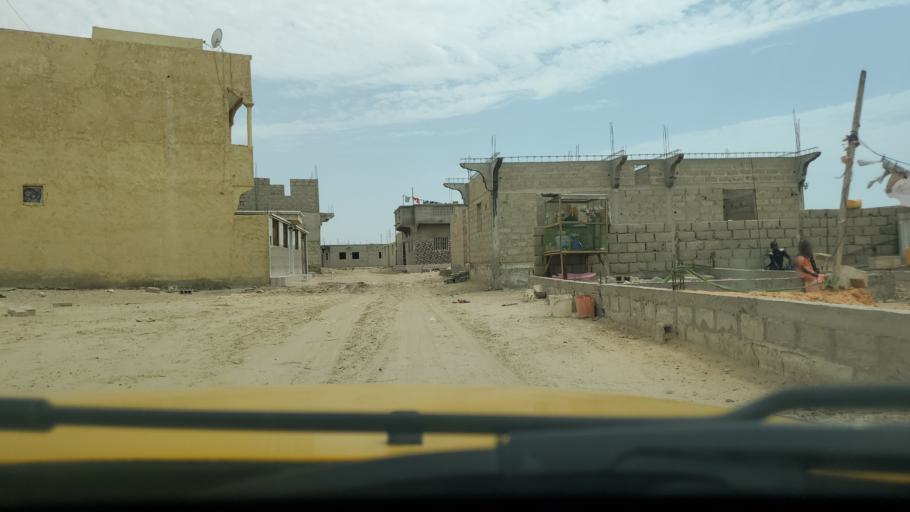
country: SN
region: Saint-Louis
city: Saint-Louis
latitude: 16.0344
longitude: -16.4619
